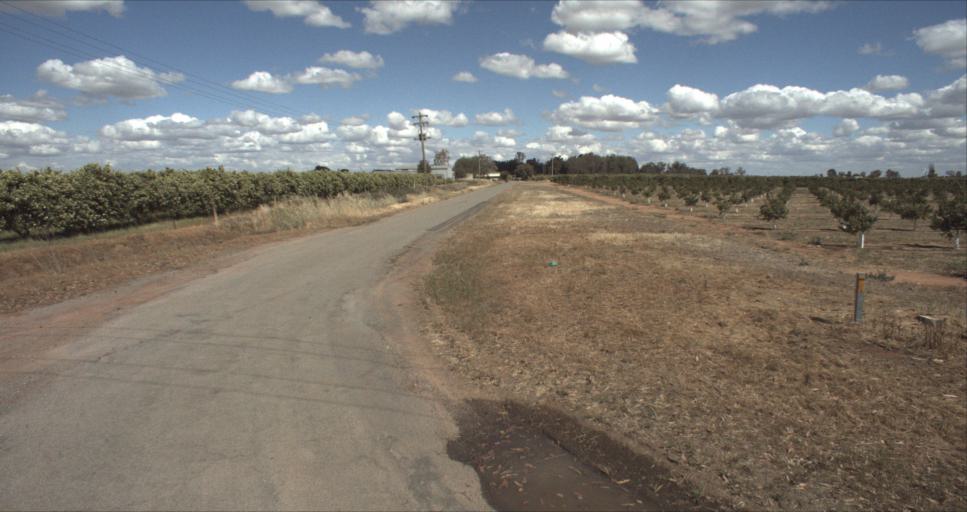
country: AU
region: New South Wales
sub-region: Leeton
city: Leeton
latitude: -34.5093
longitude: 146.2314
